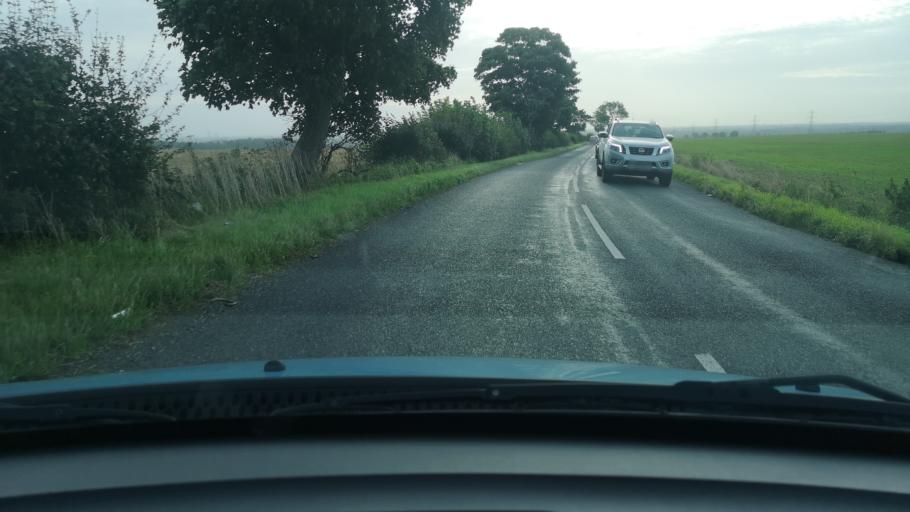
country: GB
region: England
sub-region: Doncaster
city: Campsall
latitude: 53.6184
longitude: -1.2128
